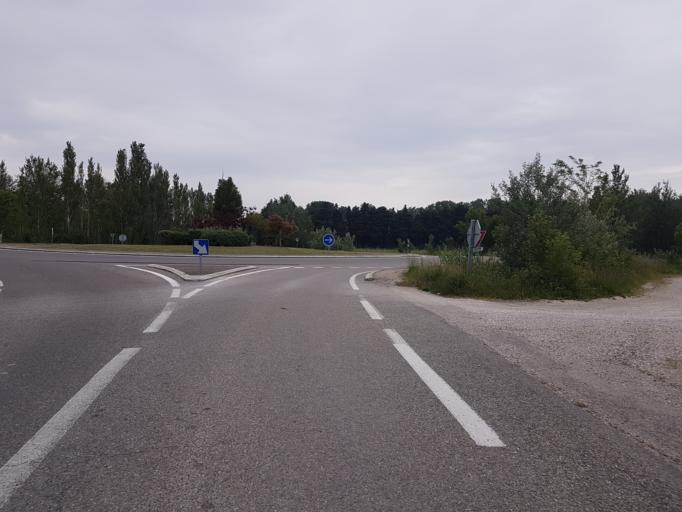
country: FR
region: Languedoc-Roussillon
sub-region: Departement du Gard
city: Roquemaure
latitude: 44.0569
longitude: 4.7771
